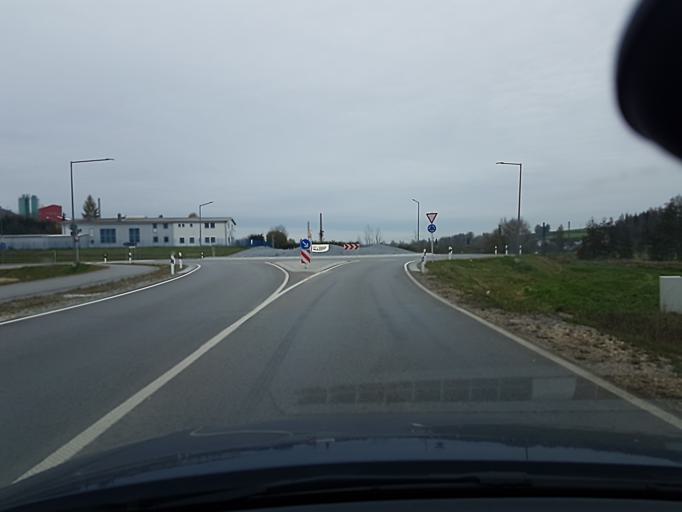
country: DE
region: Bavaria
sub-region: Lower Bavaria
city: Ergoldsbach
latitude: 48.7189
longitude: 12.1909
